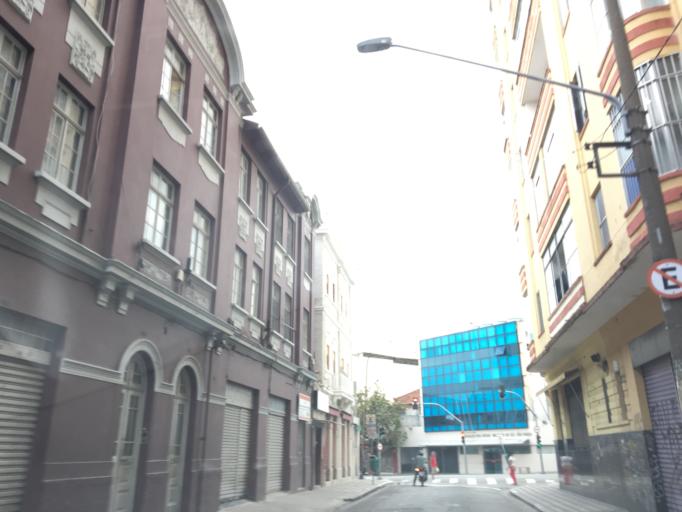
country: BR
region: Sao Paulo
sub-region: Sao Paulo
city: Sao Paulo
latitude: -23.5522
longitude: -46.6308
